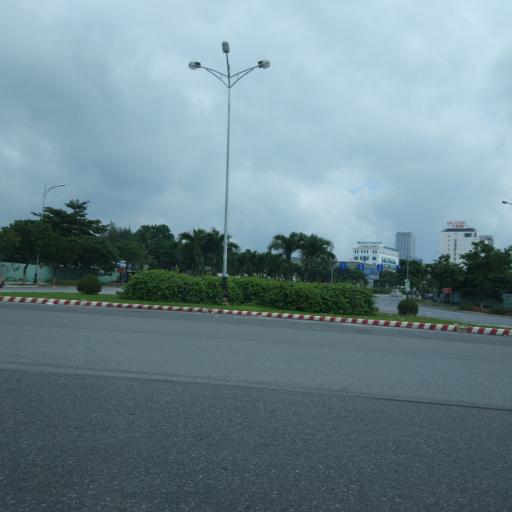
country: VN
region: Da Nang
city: Da Nang
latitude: 16.0727
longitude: 108.2308
